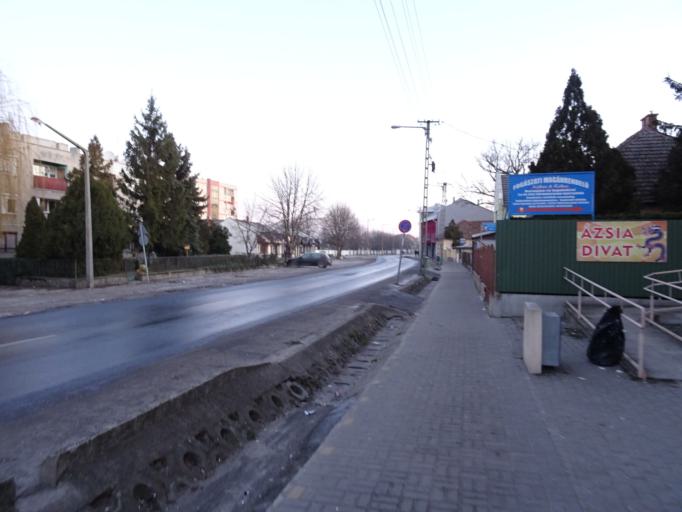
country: HU
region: Pest
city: Nagykata
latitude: 47.4118
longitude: 19.7362
